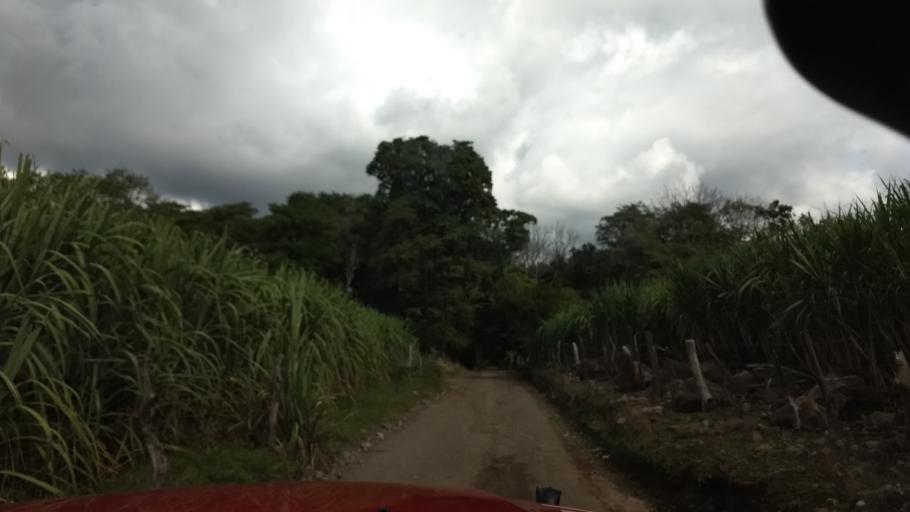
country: MX
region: Colima
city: Suchitlan
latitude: 19.4621
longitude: -103.7527
